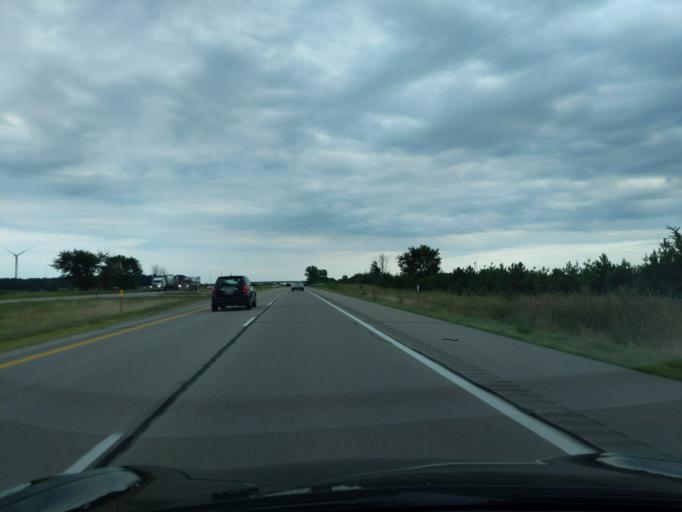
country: US
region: Michigan
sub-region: Isabella County
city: Shepherd
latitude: 43.5464
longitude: -84.6951
